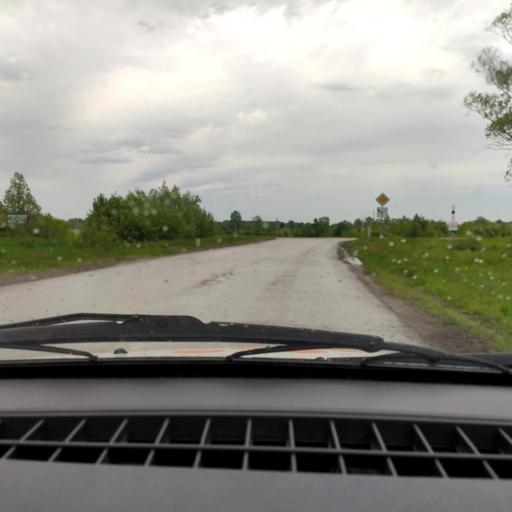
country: RU
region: Bashkortostan
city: Urman
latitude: 54.8642
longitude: 56.8412
